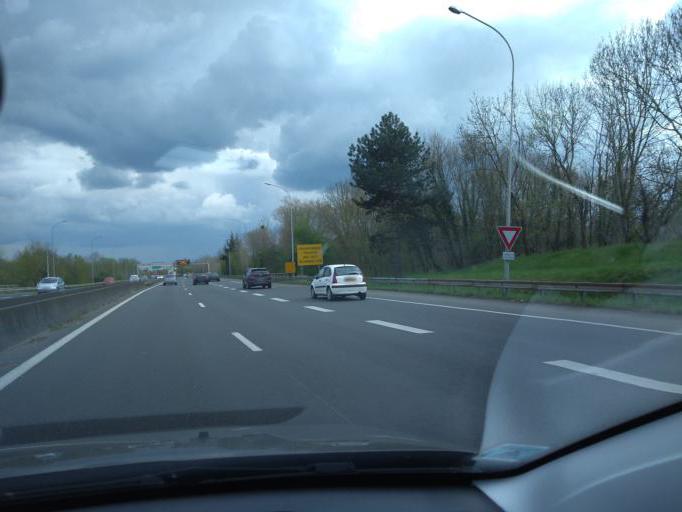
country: FR
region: Pays de la Loire
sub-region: Departement de Maine-et-Loire
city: Angers
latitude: 47.4652
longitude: -0.5780
